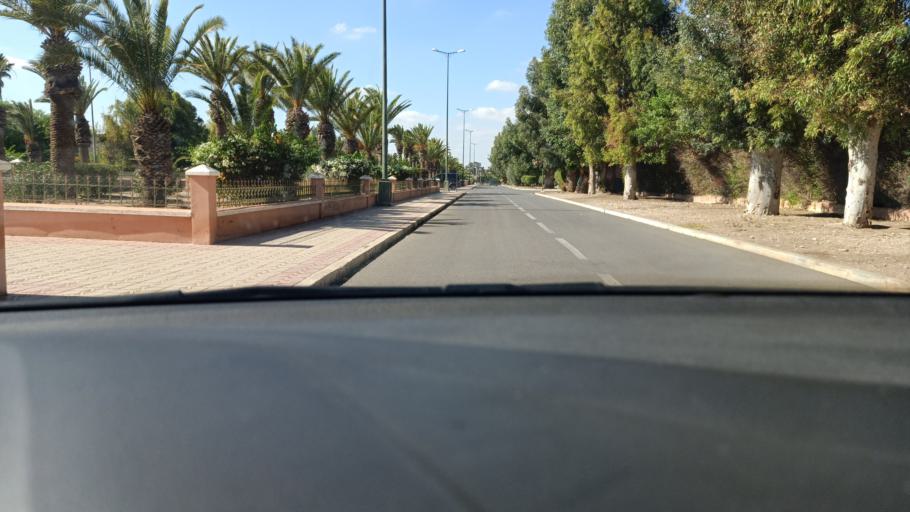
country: MA
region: Doukkala-Abda
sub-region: Safi
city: Youssoufia
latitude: 32.2455
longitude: -8.5303
